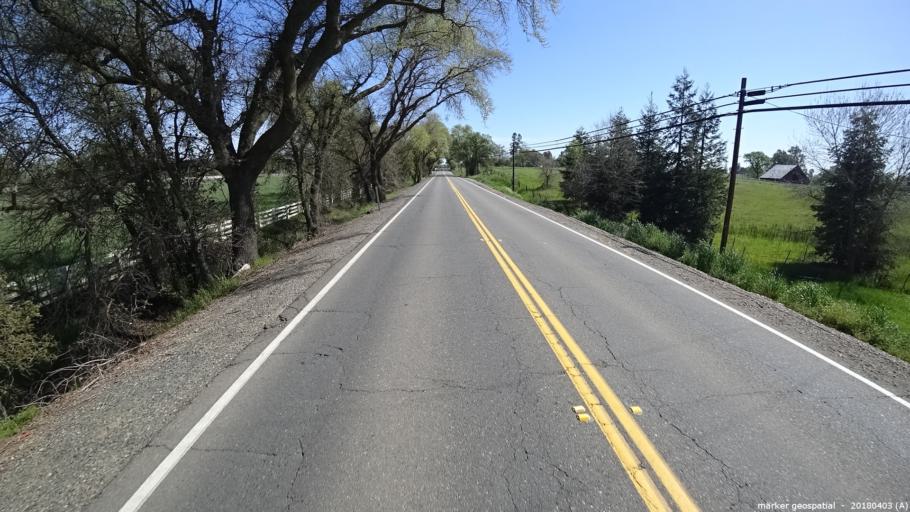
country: US
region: California
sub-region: Sacramento County
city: Wilton
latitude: 38.4192
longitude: -121.2228
